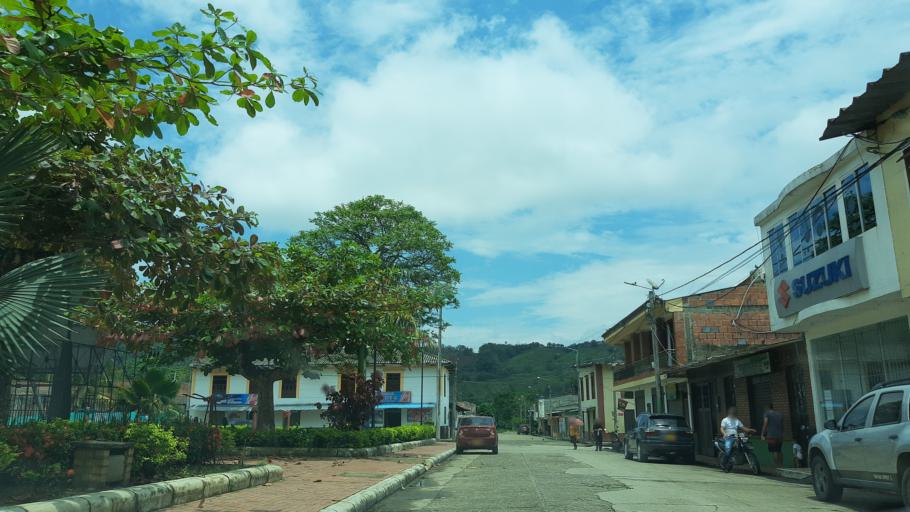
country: CO
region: Boyaca
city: San Luis de Gaceno
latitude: 4.8204
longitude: -73.1681
